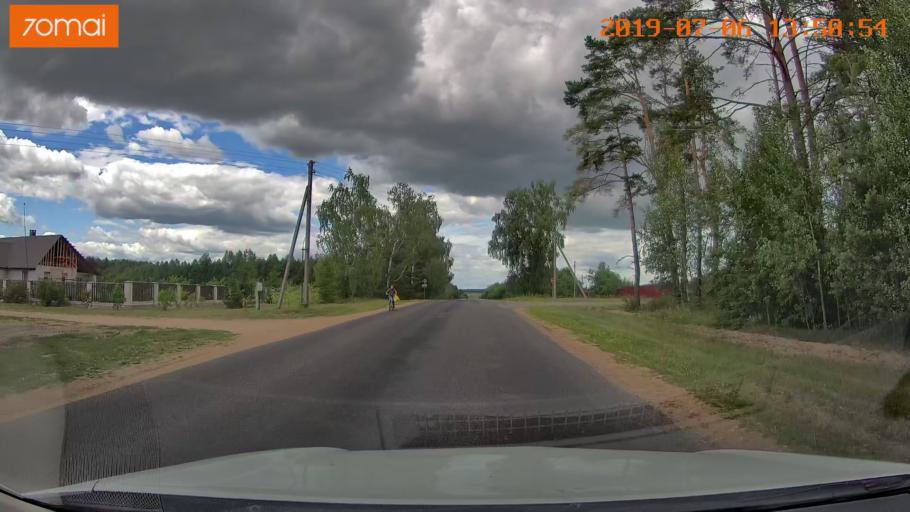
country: BY
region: Minsk
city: Ivyanyets
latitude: 53.7033
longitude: 26.8386
